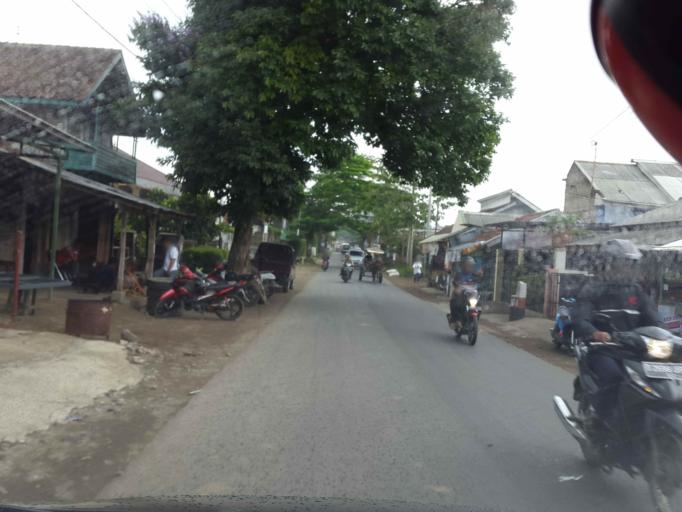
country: ID
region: West Java
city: Lembang
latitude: -6.8248
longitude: 107.6420
